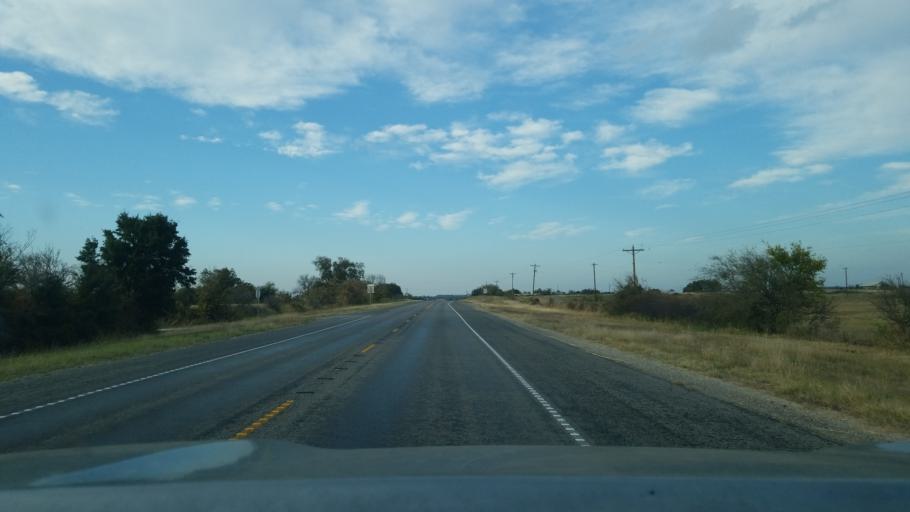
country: US
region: Texas
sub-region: Brown County
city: Lake Brownwood
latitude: 31.9866
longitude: -98.9207
